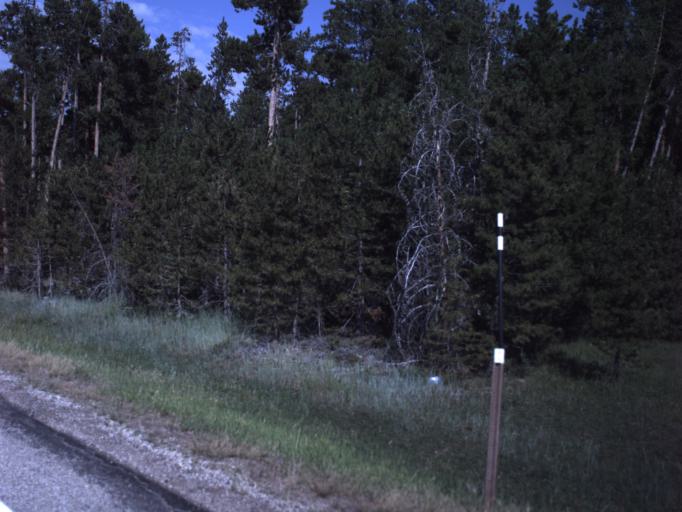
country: US
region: Utah
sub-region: Daggett County
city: Manila
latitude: 40.8411
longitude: -109.6498
